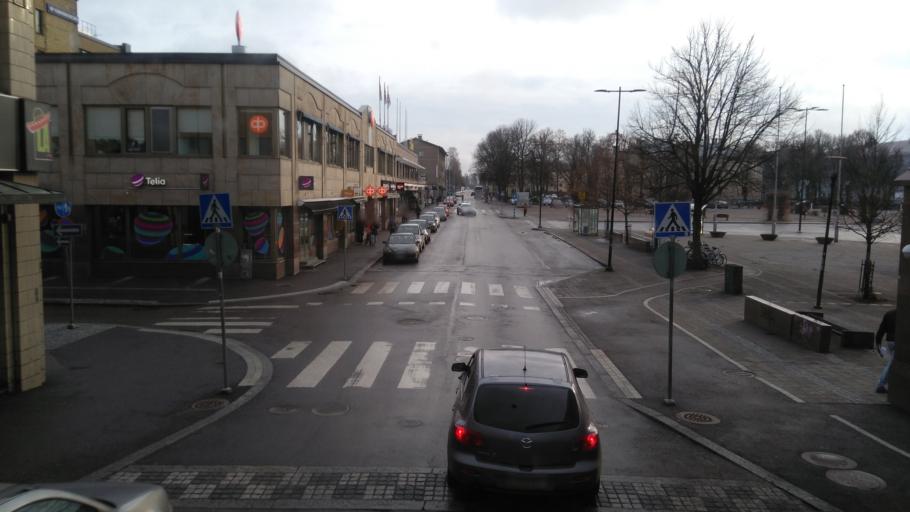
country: FI
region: Uusimaa
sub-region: Porvoo
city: Porvoo
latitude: 60.3939
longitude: 25.6647
